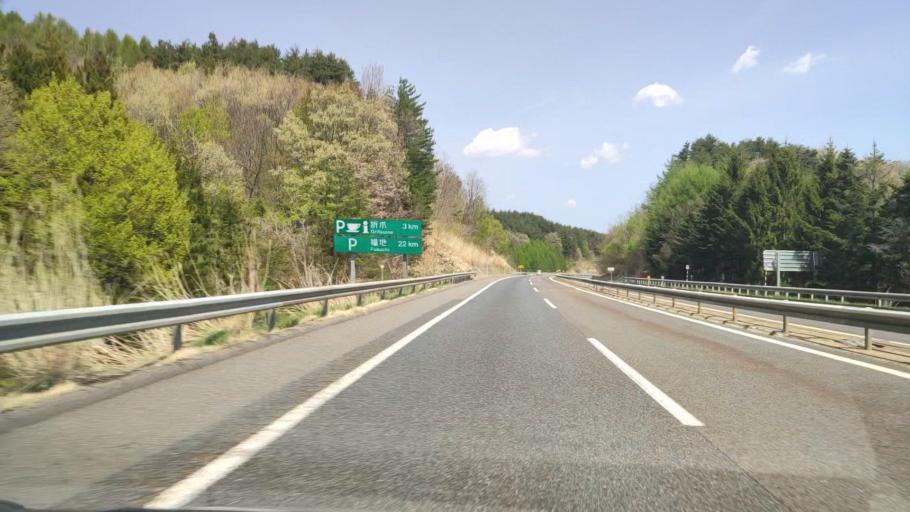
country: JP
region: Iwate
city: Ichinohe
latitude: 40.2706
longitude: 141.3992
